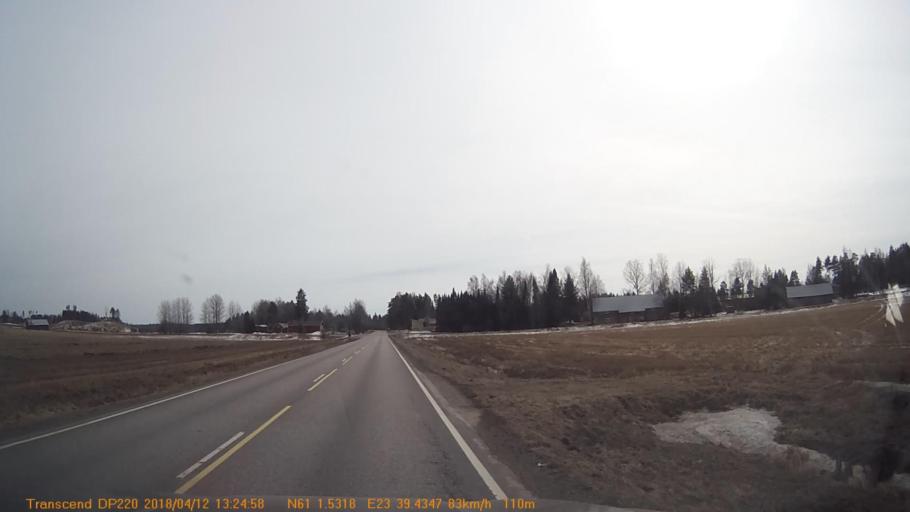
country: FI
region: Pirkanmaa
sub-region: Etelae-Pirkanmaa
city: Kylmaekoski
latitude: 61.0245
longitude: 23.6581
